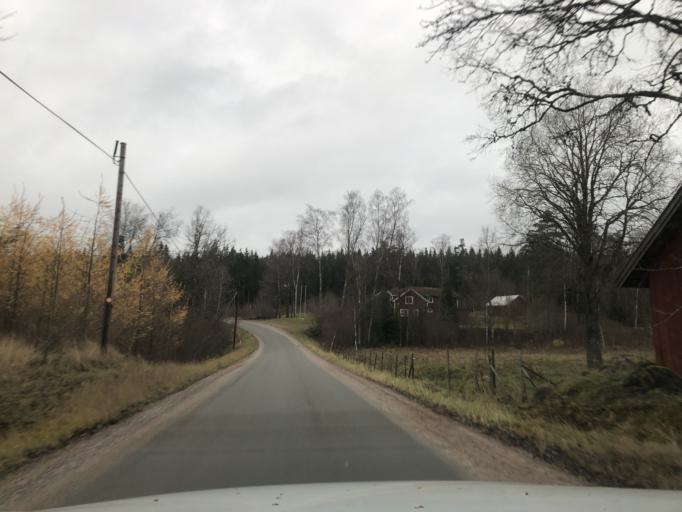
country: SE
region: Vaestra Goetaland
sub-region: Ulricehamns Kommun
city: Ulricehamn
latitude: 57.8635
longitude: 13.5696
